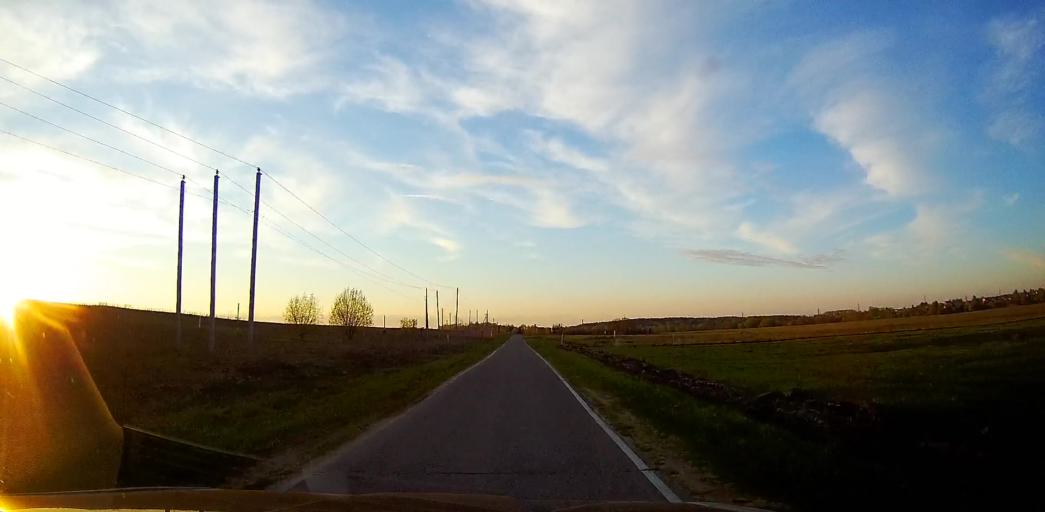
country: RU
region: Moskovskaya
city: Peski
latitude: 55.2217
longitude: 38.7370
